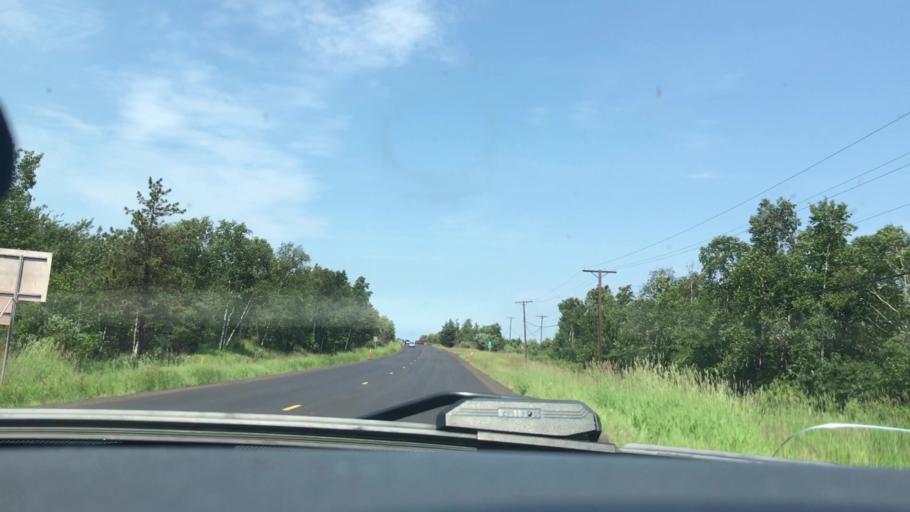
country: US
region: Minnesota
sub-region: Lake County
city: Silver Bay
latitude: 47.2782
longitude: -91.2726
